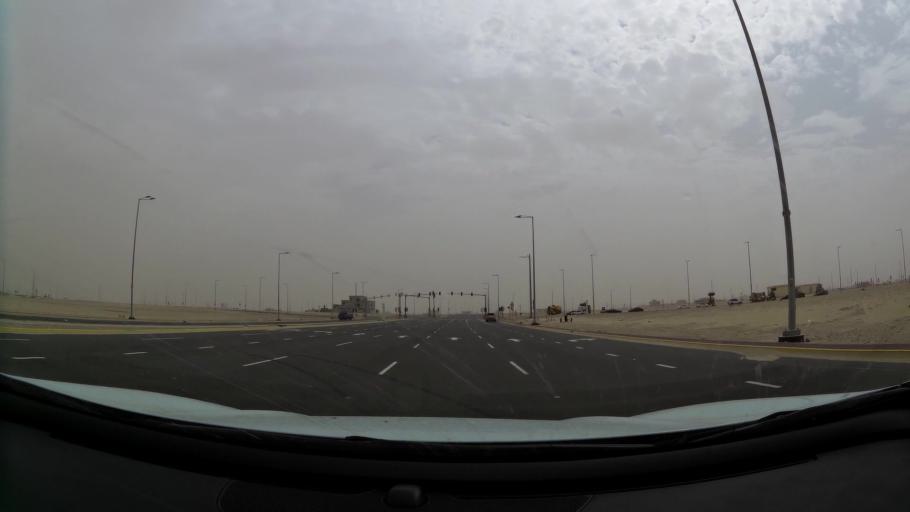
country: AE
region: Abu Dhabi
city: Abu Dhabi
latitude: 24.3711
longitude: 54.7457
